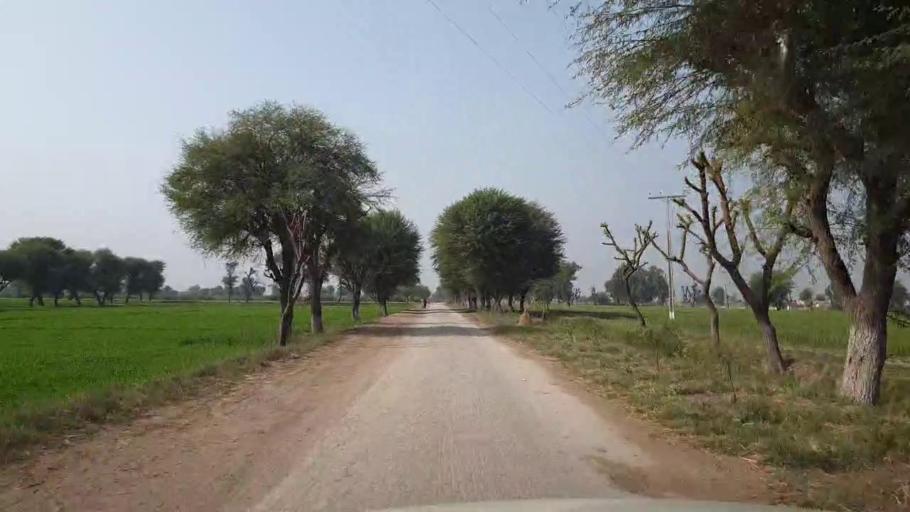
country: PK
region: Sindh
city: Umarkot
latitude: 25.4351
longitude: 69.7171
